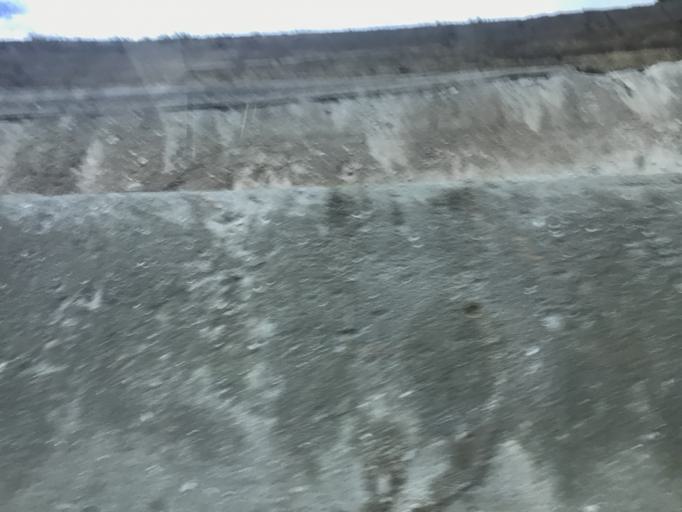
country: GT
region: Chimaltenango
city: El Tejar
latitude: 14.6367
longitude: -90.7936
